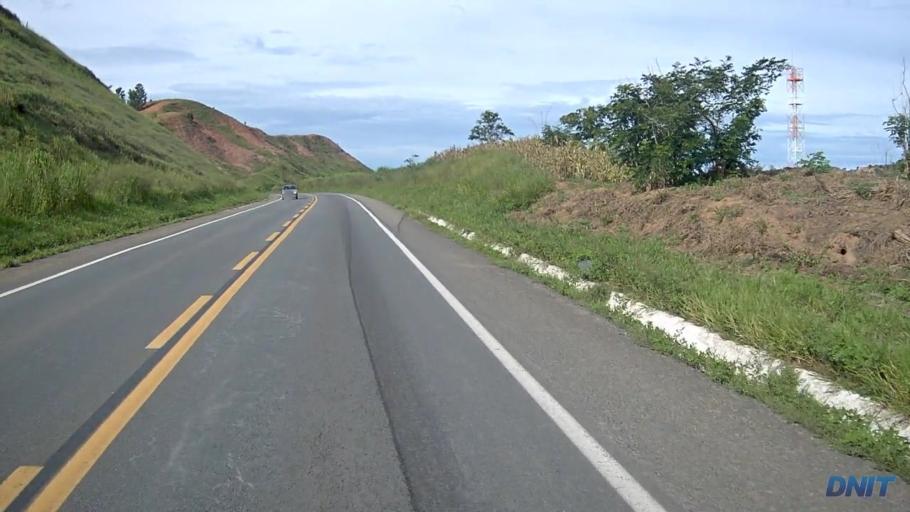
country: BR
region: Minas Gerais
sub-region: Belo Oriente
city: Belo Oriente
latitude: -19.1773
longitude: -42.2565
